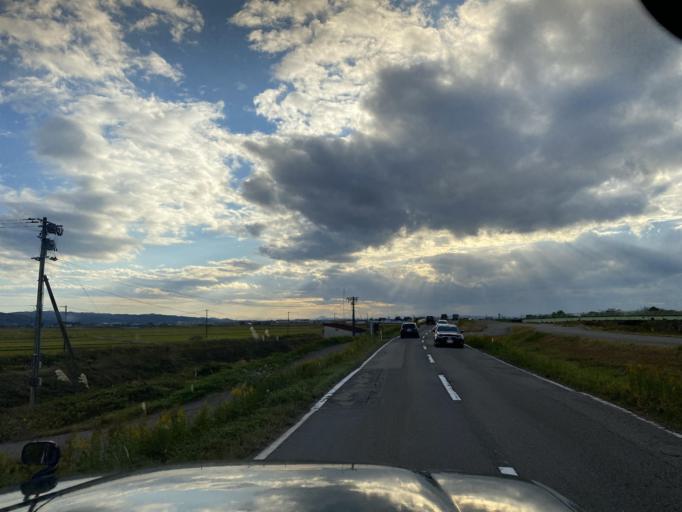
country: JP
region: Niigata
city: Kamo
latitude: 37.6696
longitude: 139.0093
